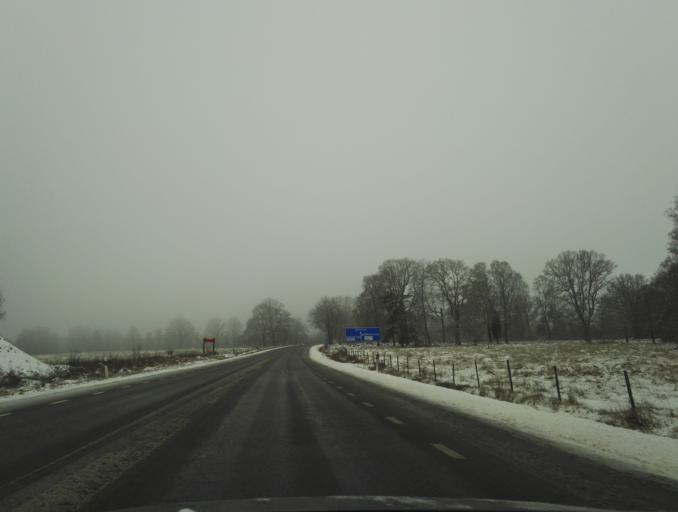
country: SE
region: Kronoberg
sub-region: Vaxjo Kommun
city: Vaexjoe
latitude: 56.8706
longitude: 14.7402
